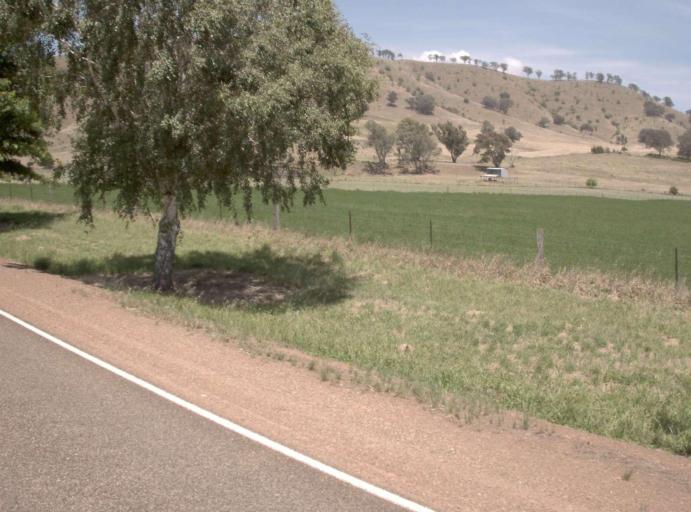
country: AU
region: Victoria
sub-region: East Gippsland
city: Bairnsdale
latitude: -37.2510
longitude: 147.7120
